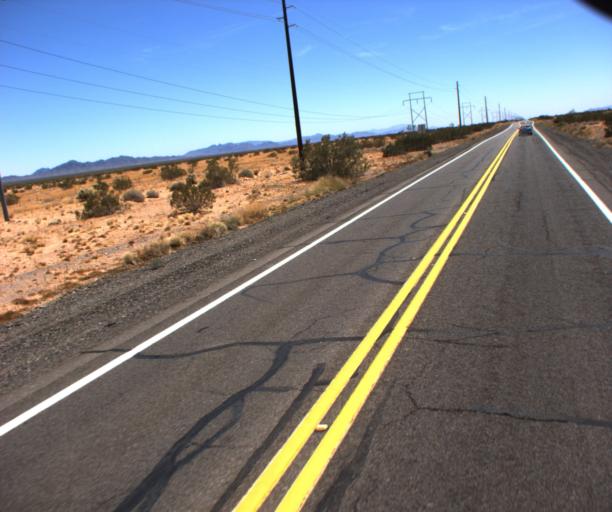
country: US
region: Arizona
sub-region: La Paz County
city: Parker
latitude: 33.9460
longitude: -114.2169
